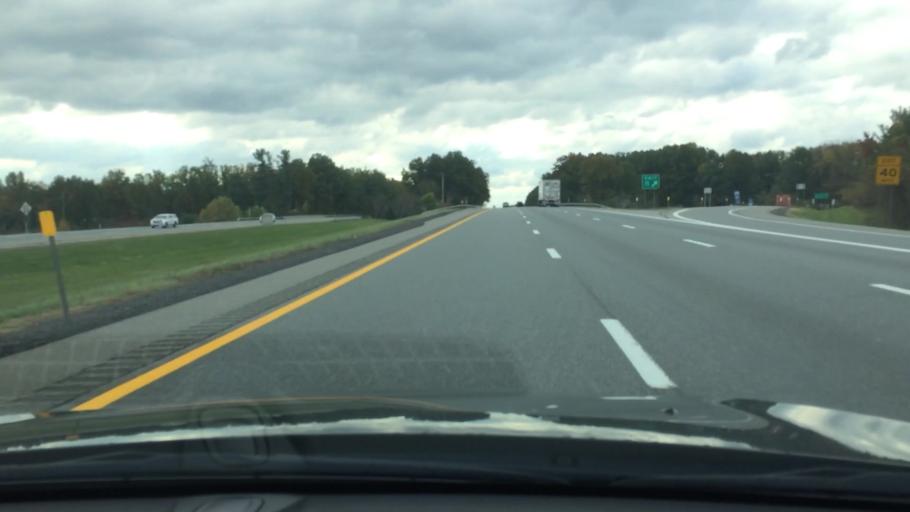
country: US
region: New York
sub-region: Saratoga County
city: Country Knolls
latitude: 42.9391
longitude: -73.8050
